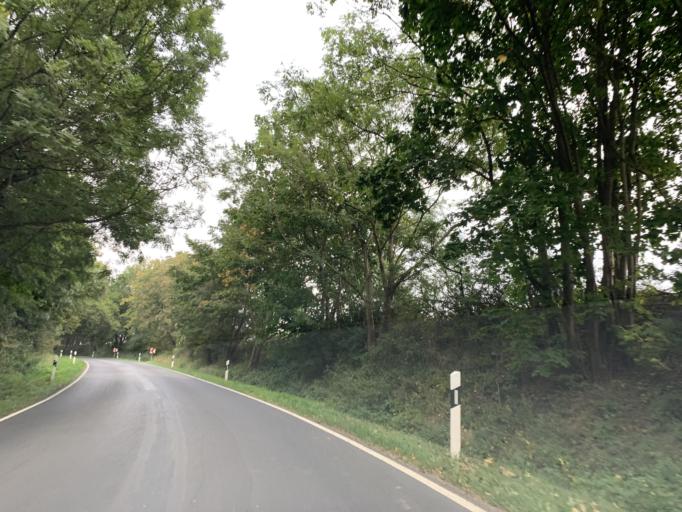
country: DE
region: Mecklenburg-Vorpommern
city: Loitz
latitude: 53.3308
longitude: 13.4945
